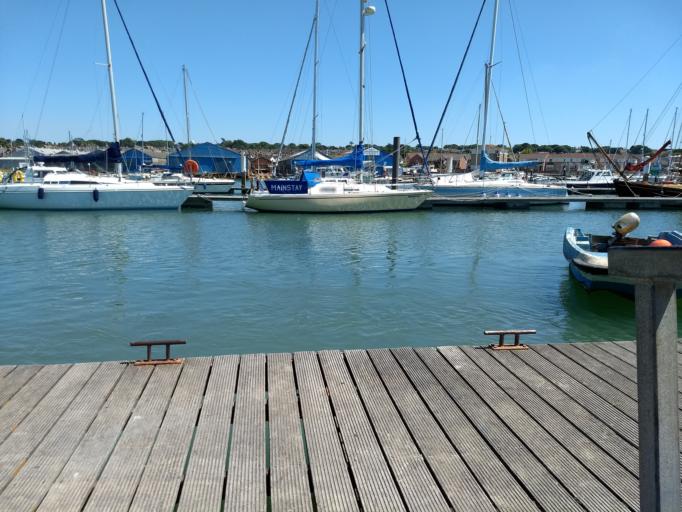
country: GB
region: England
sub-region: Isle of Wight
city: East Cowes
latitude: 50.7539
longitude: -1.2937
